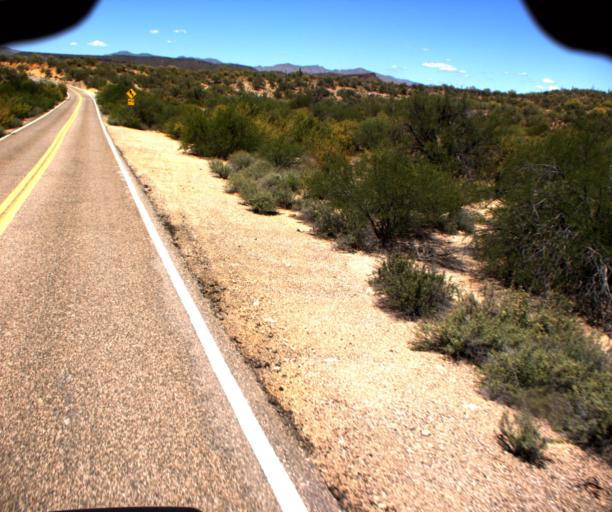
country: US
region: Arizona
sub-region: Yavapai County
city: Bagdad
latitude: 34.4723
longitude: -113.0531
